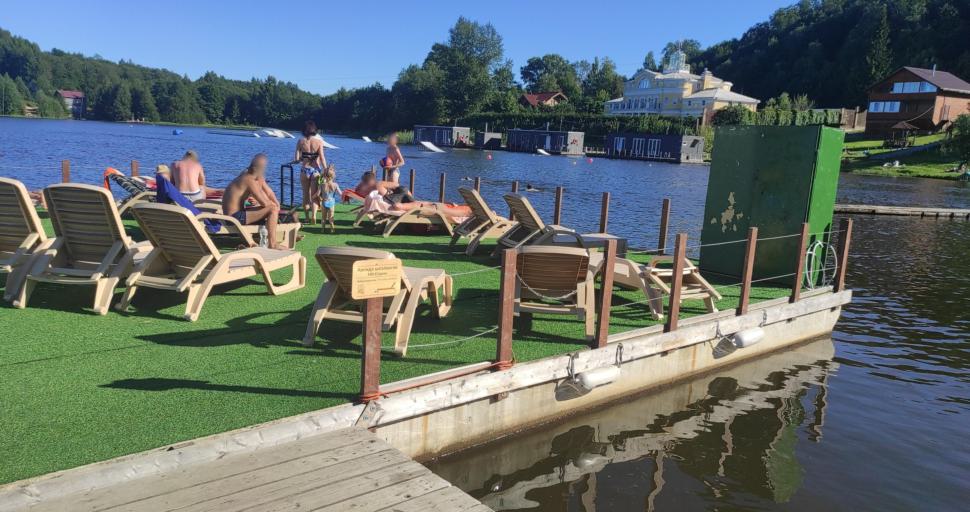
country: RU
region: Leningrad
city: Toksovo
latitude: 60.1560
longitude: 30.5540
